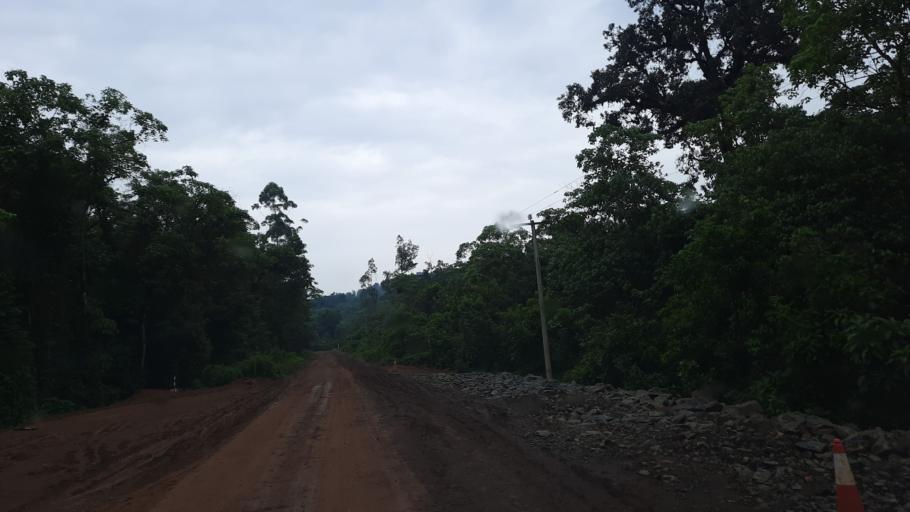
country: ET
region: Oromiya
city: Gore
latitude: 7.8696
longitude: 35.4801
